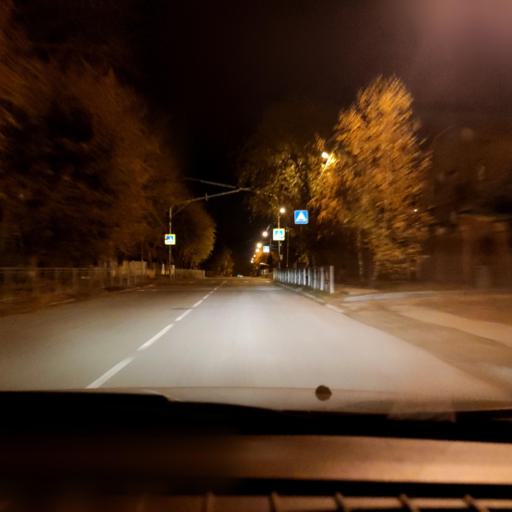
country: RU
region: Samara
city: Tol'yatti
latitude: 53.5345
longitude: 49.4037
